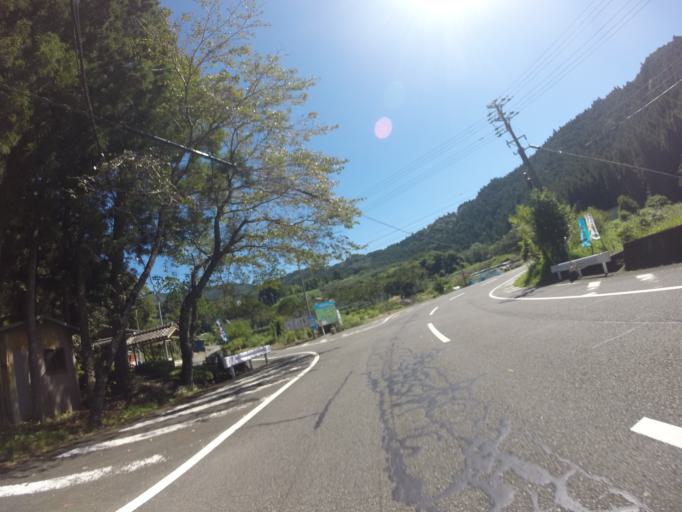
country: JP
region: Shizuoka
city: Kanaya
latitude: 34.9266
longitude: 138.1346
